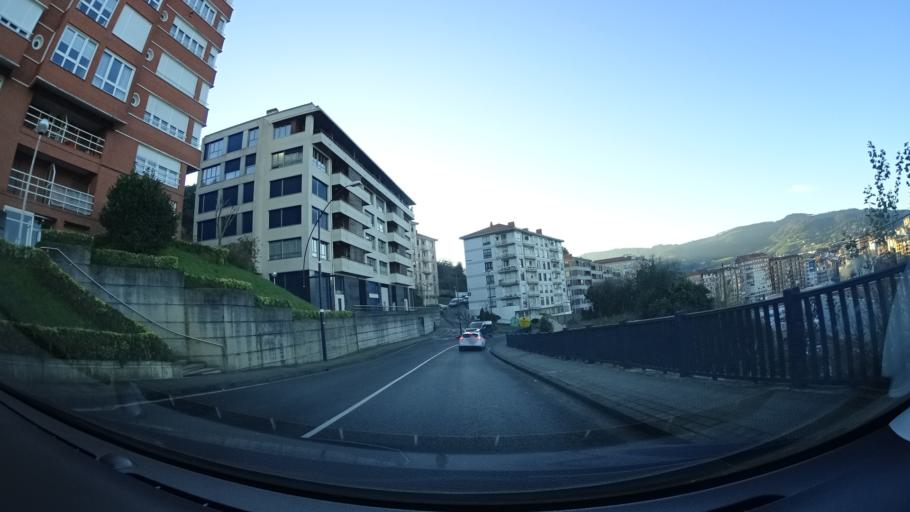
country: ES
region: Basque Country
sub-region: Bizkaia
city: Bermeo
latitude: 43.4167
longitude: -2.7198
